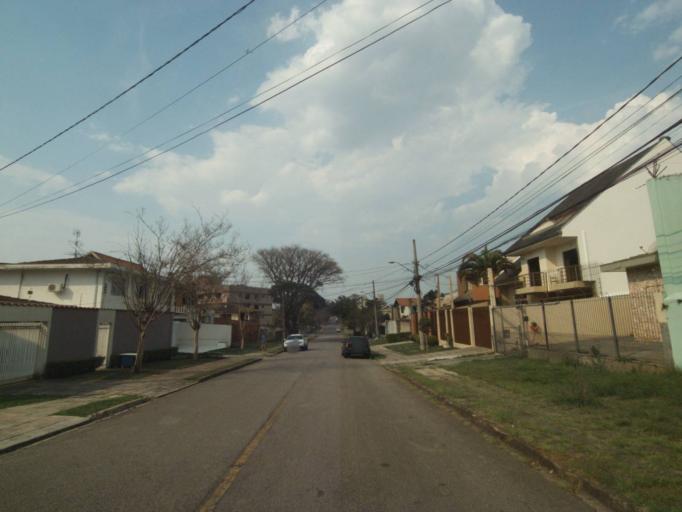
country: BR
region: Parana
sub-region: Curitiba
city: Curitiba
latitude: -25.4607
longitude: -49.2642
